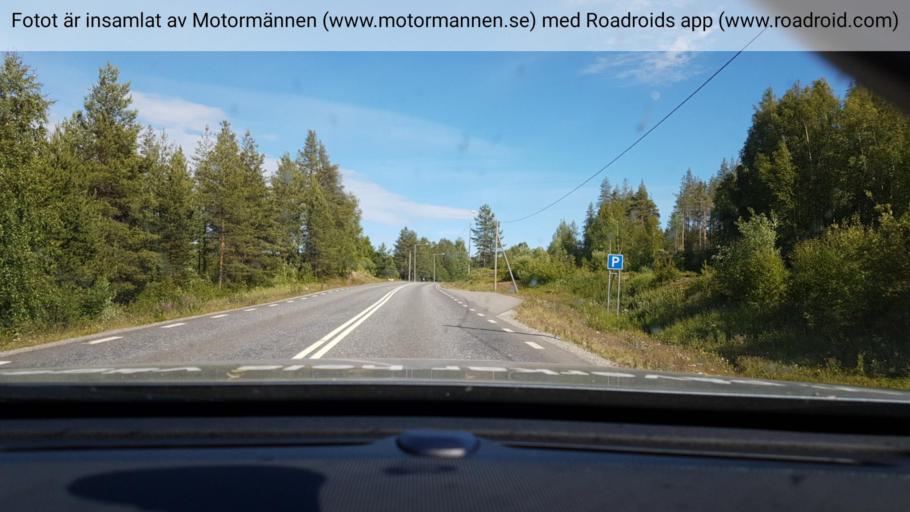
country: SE
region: Vaesterbotten
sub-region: Lycksele Kommun
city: Soderfors
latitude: 64.7019
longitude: 18.3563
